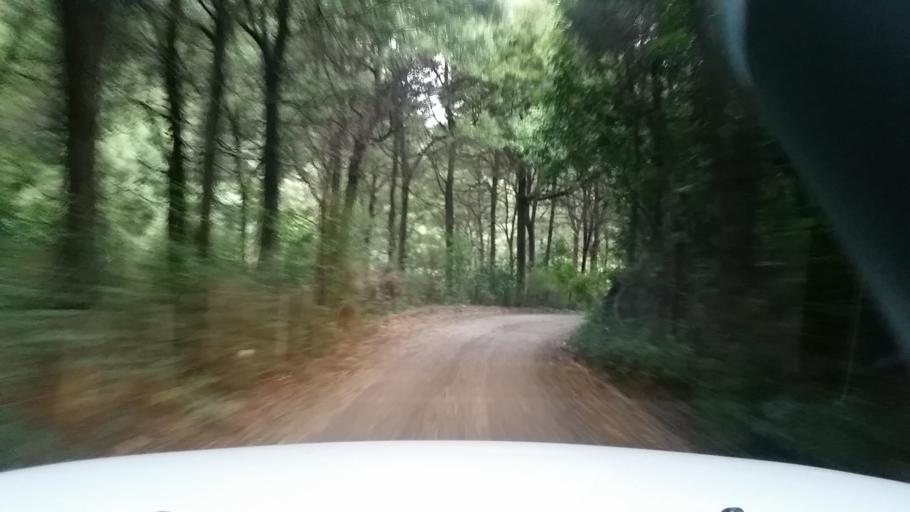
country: NZ
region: Canterbury
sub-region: Christchurch City
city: Christchurch
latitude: -43.7273
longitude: 172.7838
